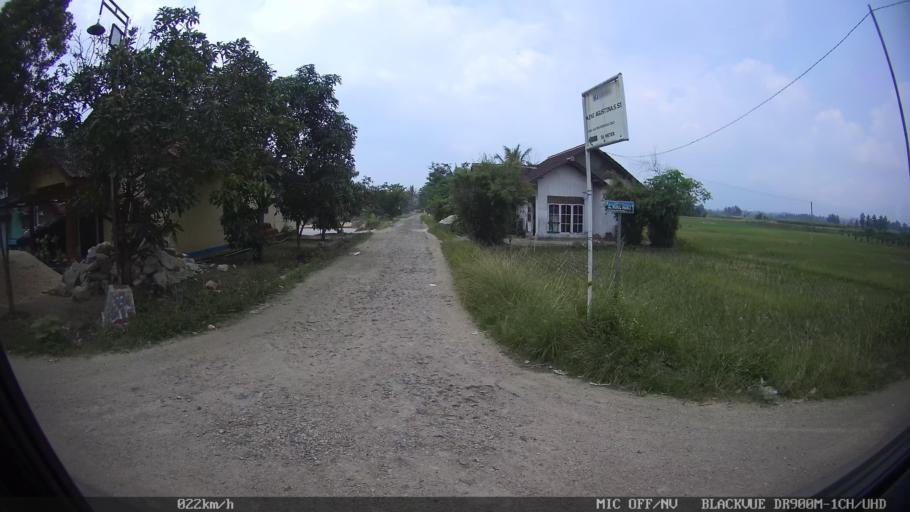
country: ID
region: Lampung
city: Gadingrejo
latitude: -5.3868
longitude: 105.0433
